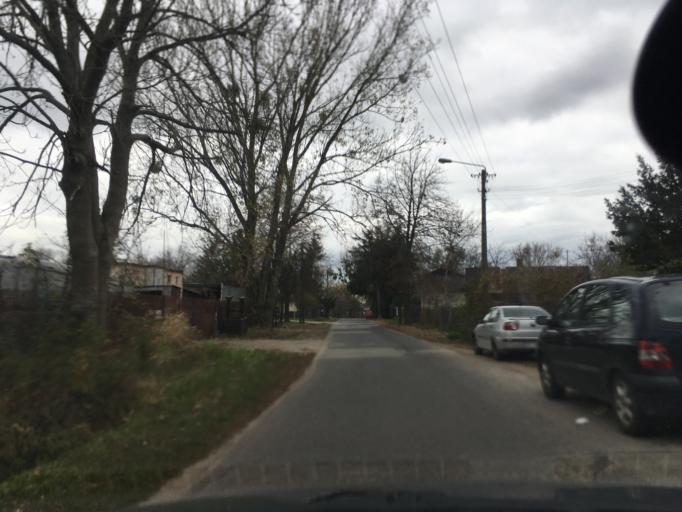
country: PL
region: Lodz Voivodeship
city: Zabia Wola
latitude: 52.0307
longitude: 20.6926
